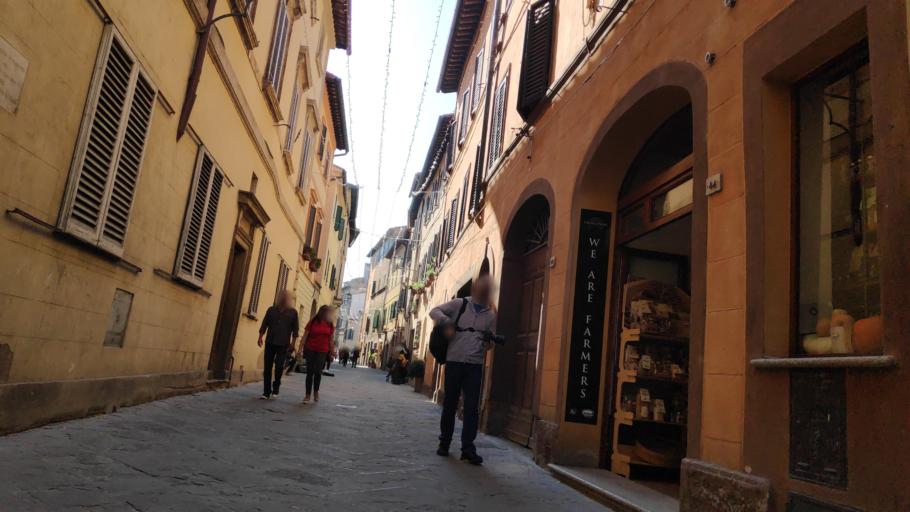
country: IT
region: Tuscany
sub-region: Provincia di Siena
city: Montepulciano
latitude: 43.0921
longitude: 11.7819
